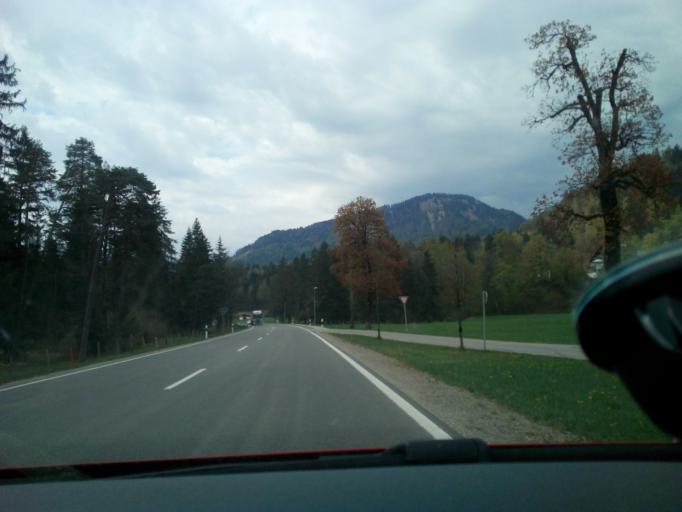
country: DE
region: Bavaria
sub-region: Upper Bavaria
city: Kreuth
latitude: 47.6529
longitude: 11.7477
